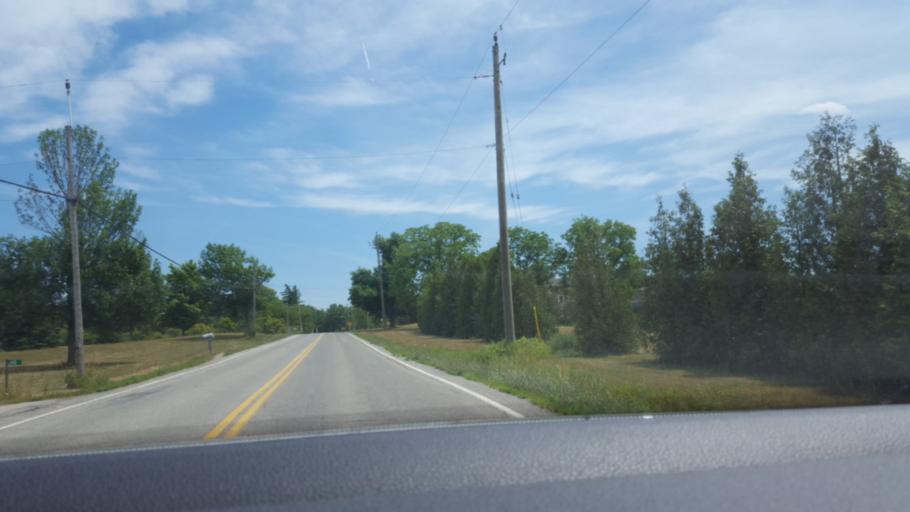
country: CA
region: Ontario
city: Oakville
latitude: 43.1833
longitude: -79.5652
